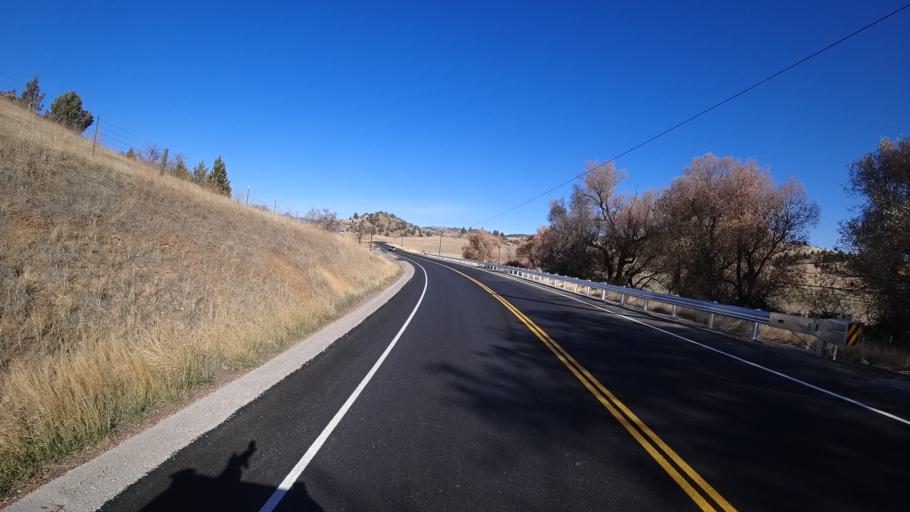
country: US
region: California
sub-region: Siskiyou County
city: Montague
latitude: 41.8537
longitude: -122.4649
